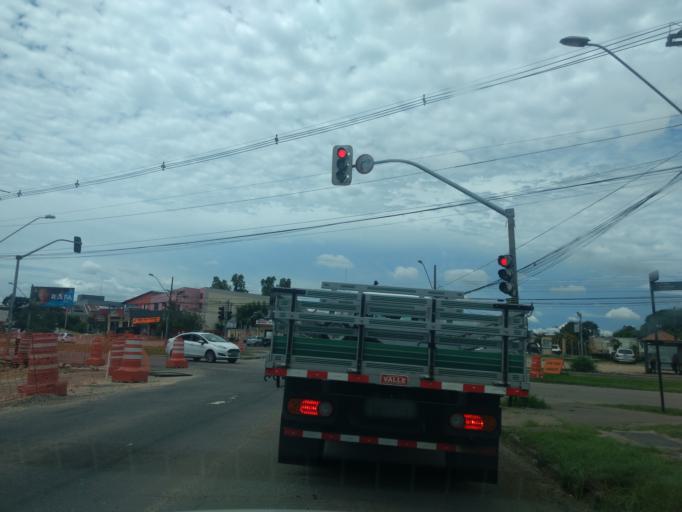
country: BR
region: Parana
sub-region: Pinhais
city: Pinhais
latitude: -25.4298
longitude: -49.2137
